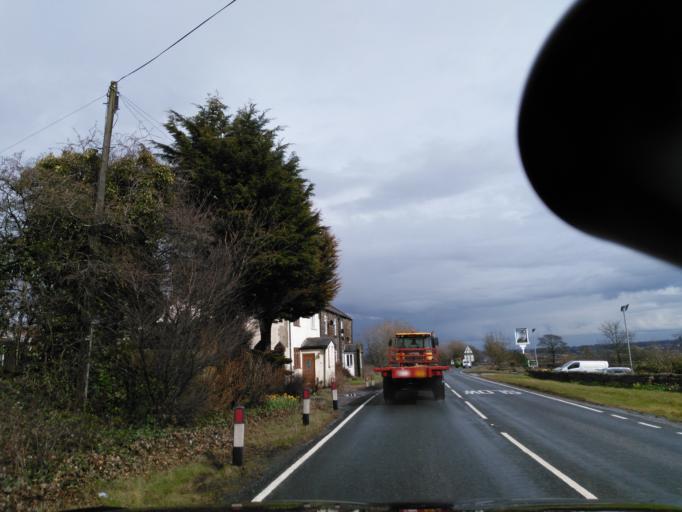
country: GB
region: England
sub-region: North Yorkshire
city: Harrogate
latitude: 54.0091
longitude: -1.5951
